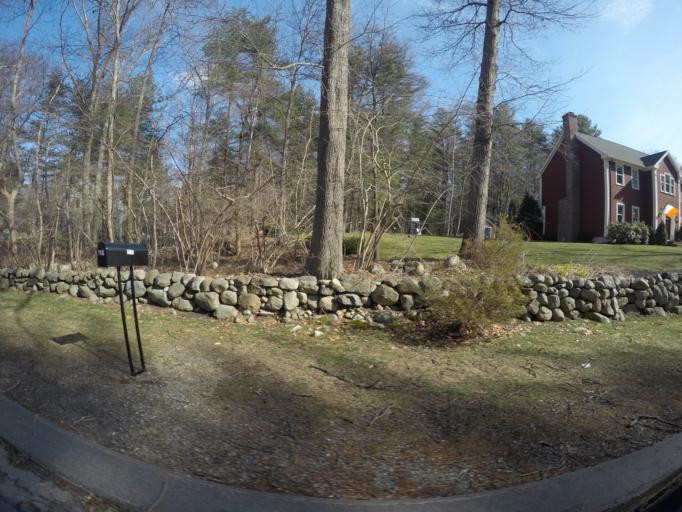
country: US
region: Massachusetts
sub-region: Bristol County
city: Easton
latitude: 42.0207
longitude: -71.1454
